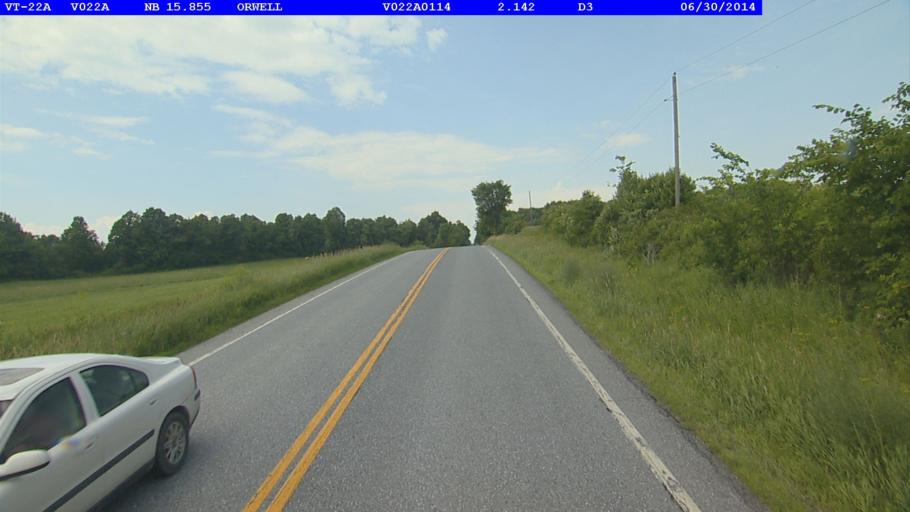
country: US
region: New York
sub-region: Essex County
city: Ticonderoga
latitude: 43.7879
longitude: -73.3067
